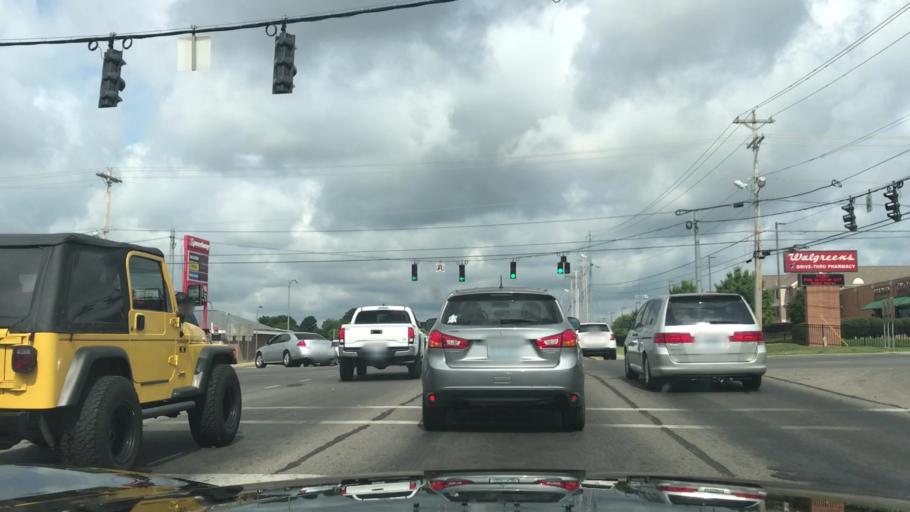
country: US
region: Kentucky
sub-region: Warren County
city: Bowling Green
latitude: 36.9622
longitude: -86.4676
